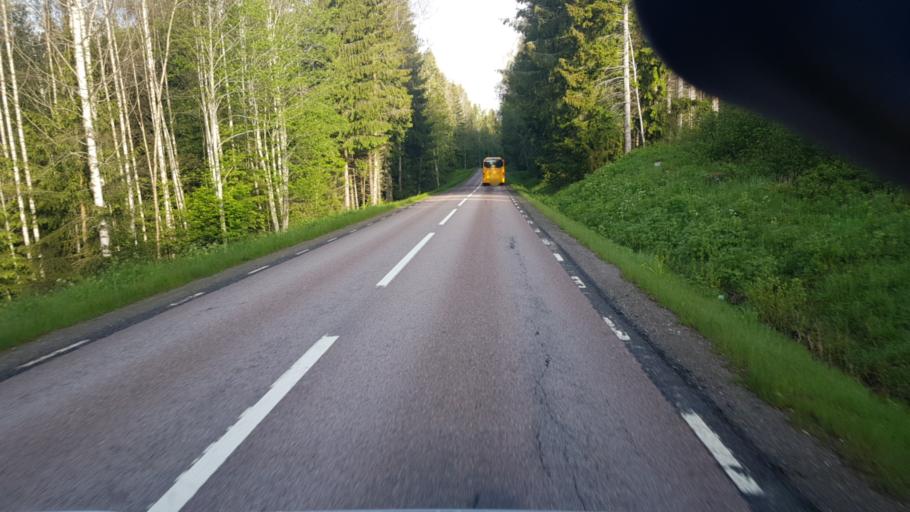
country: SE
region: Vaermland
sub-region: Eda Kommun
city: Amotfors
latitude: 59.7715
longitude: 12.3174
